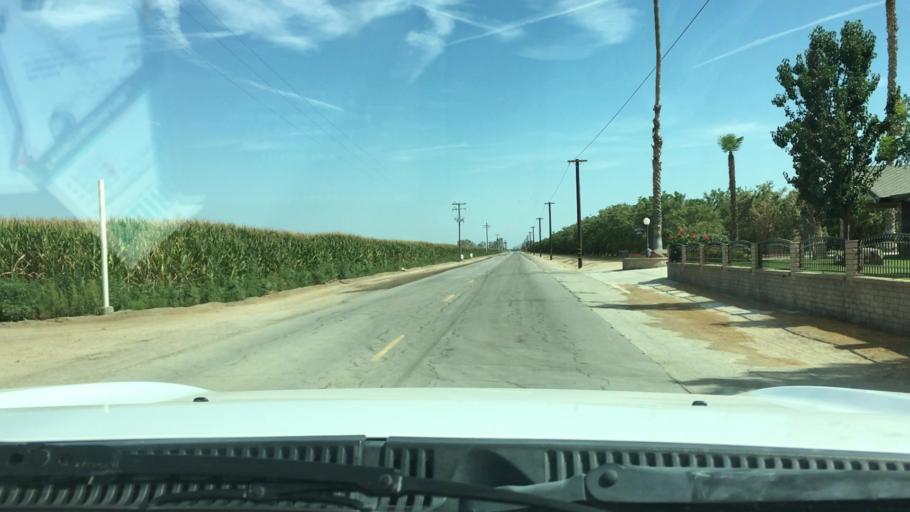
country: US
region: California
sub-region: Kern County
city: Buttonwillow
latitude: 35.4204
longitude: -119.3763
